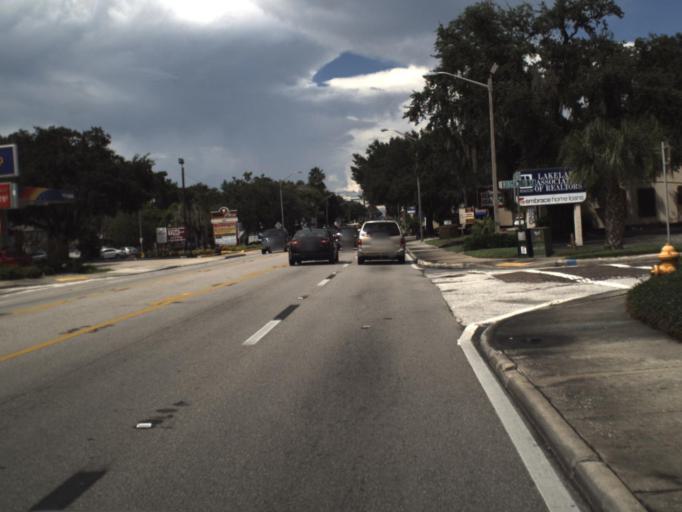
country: US
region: Florida
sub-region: Polk County
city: Lakeland
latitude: 28.0339
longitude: -81.9571
